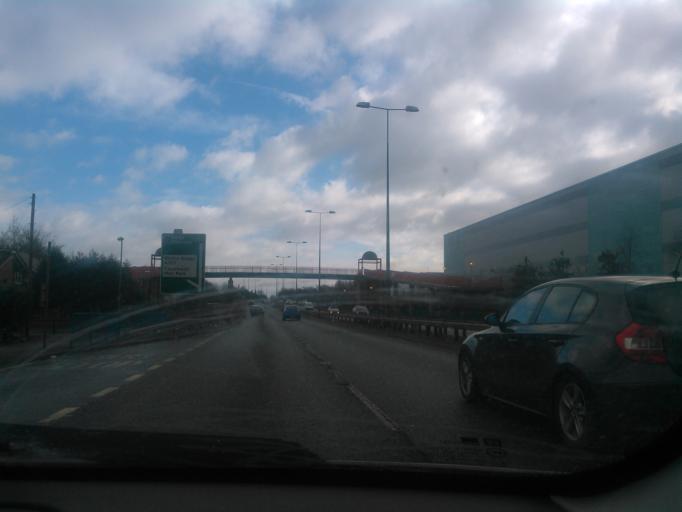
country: GB
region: England
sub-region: Staffordshire
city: Longton
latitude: 52.9750
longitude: -2.0933
